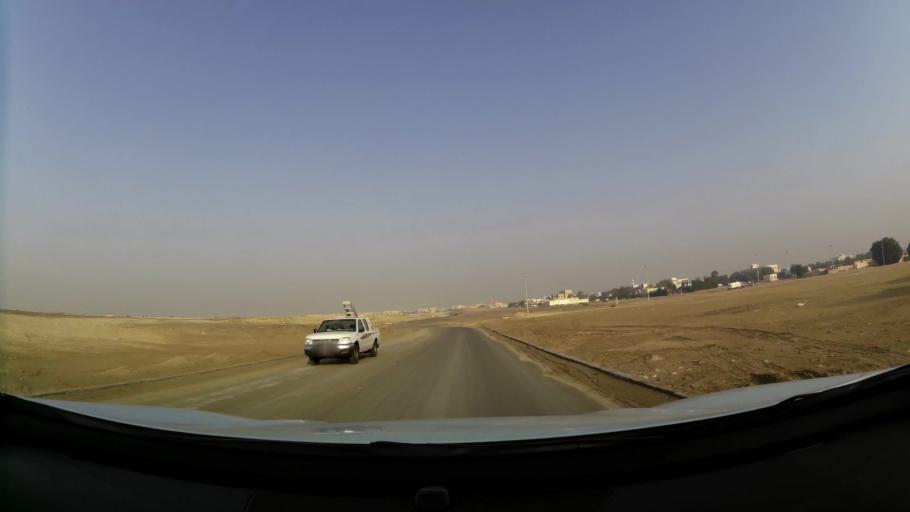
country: AE
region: Abu Dhabi
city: Abu Dhabi
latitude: 24.2817
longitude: 54.6413
